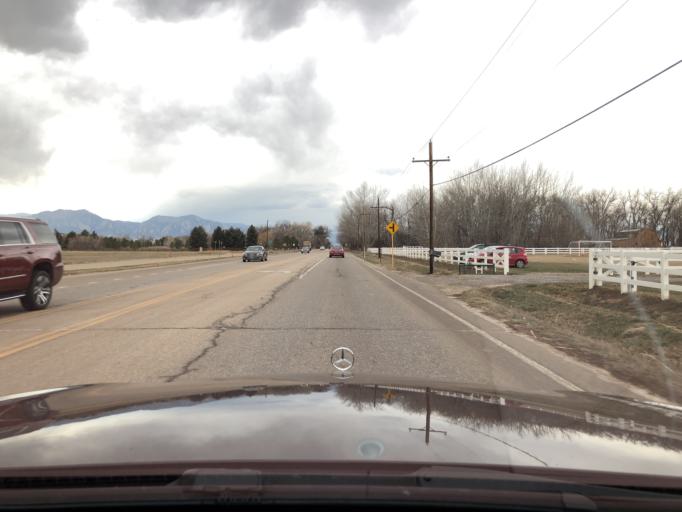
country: US
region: Colorado
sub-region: Boulder County
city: Louisville
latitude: 40.0147
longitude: -105.1386
